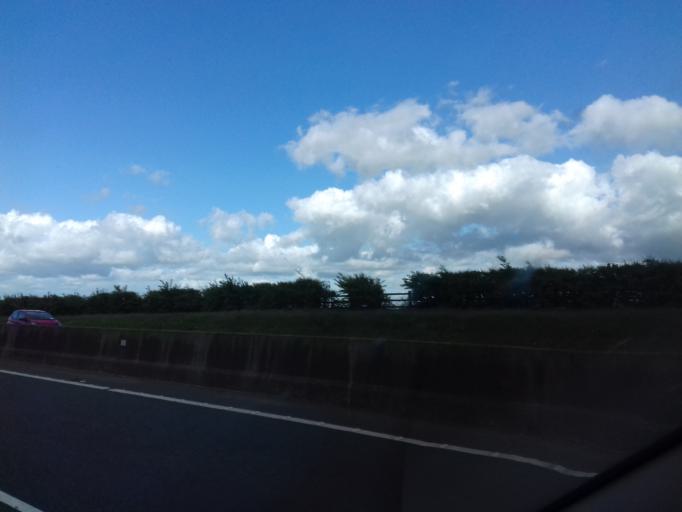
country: IE
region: Leinster
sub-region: Kilkenny
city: Kilkenny
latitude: 52.5547
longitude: -7.2467
